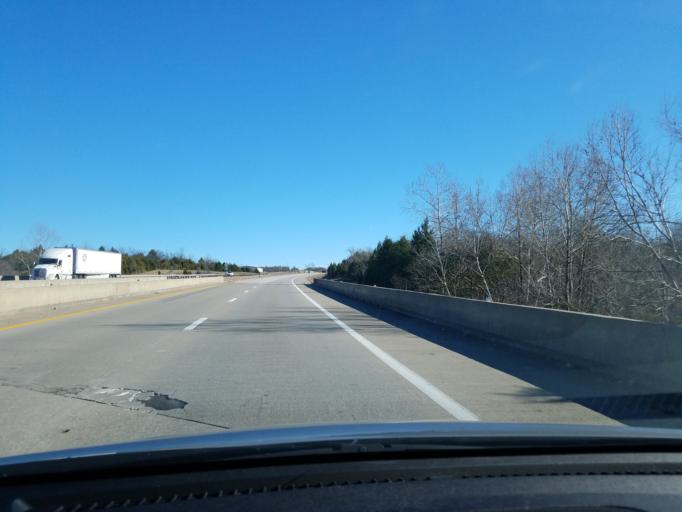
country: US
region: Missouri
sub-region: Pulaski County
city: Richland
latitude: 37.7605
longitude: -92.5190
